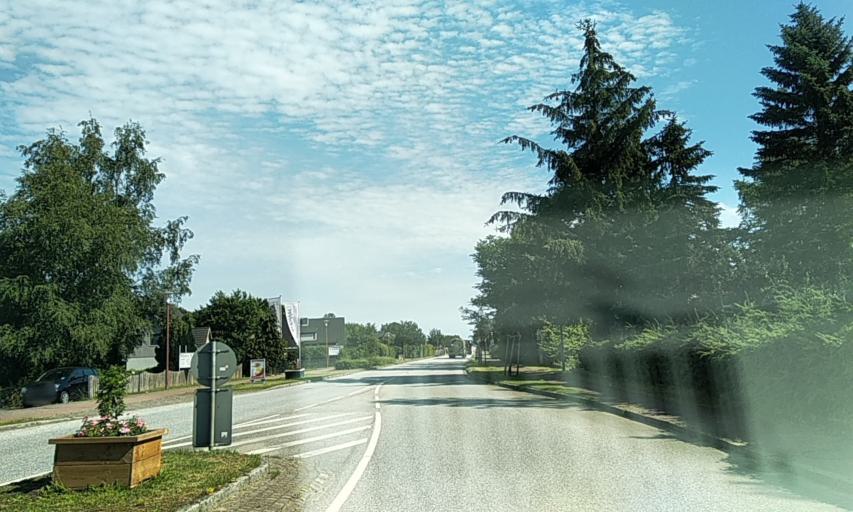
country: DE
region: Schleswig-Holstein
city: Jagel
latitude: 54.4572
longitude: 9.5376
